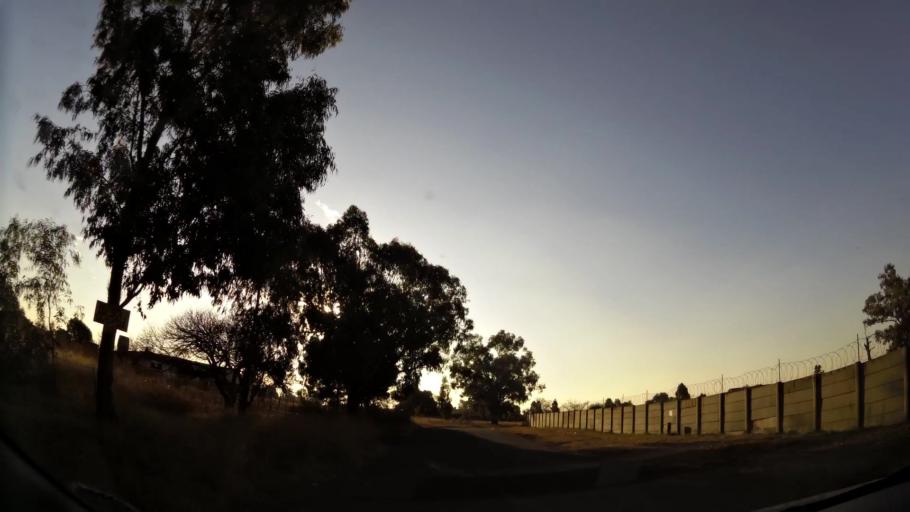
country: ZA
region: Gauteng
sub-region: West Rand District Municipality
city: Randfontein
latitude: -26.2143
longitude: 27.6432
